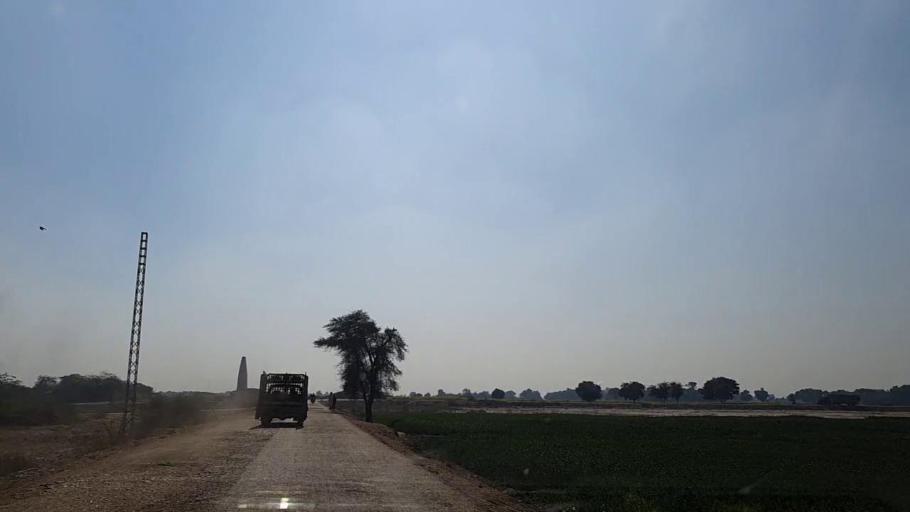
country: PK
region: Sindh
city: Sakrand
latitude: 26.2925
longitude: 68.1081
